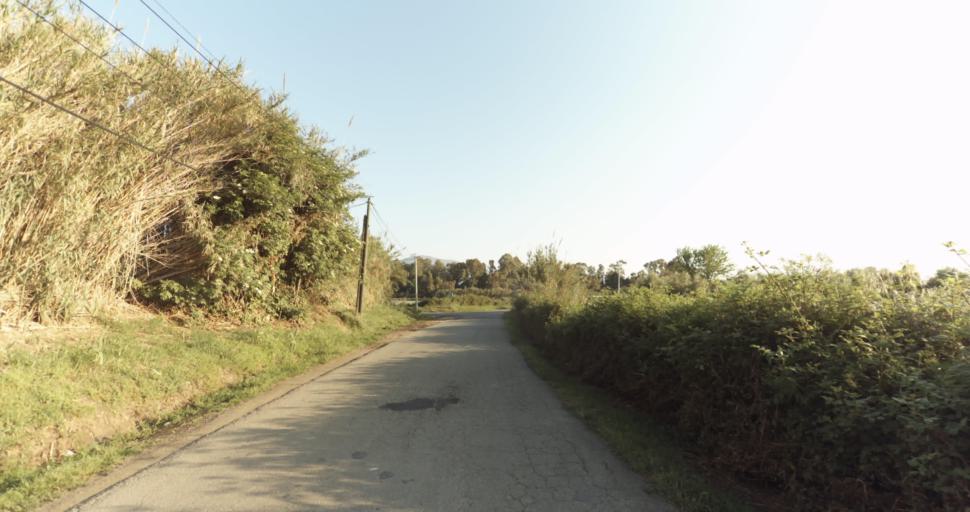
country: FR
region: Corsica
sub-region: Departement de la Haute-Corse
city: Biguglia
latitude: 42.6105
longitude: 9.4425
